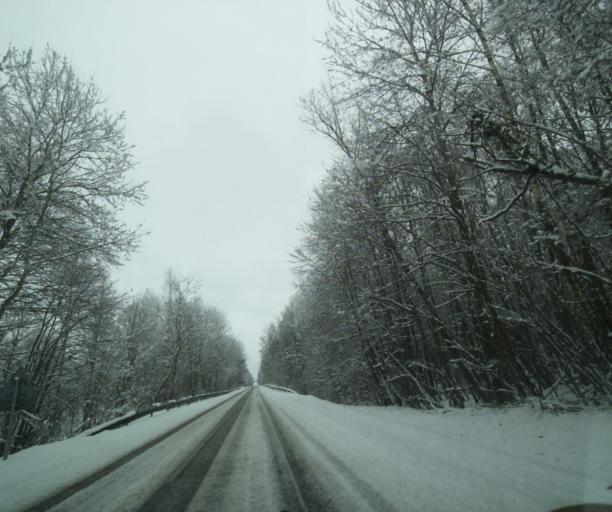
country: FR
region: Champagne-Ardenne
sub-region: Departement de la Haute-Marne
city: Montier-en-Der
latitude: 48.5298
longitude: 4.7893
